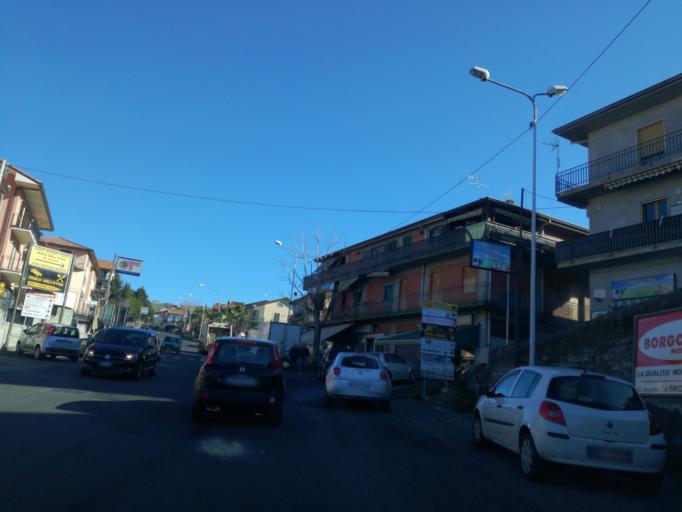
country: IT
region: Sicily
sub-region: Catania
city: Bronte
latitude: 37.7913
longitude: 14.8422
